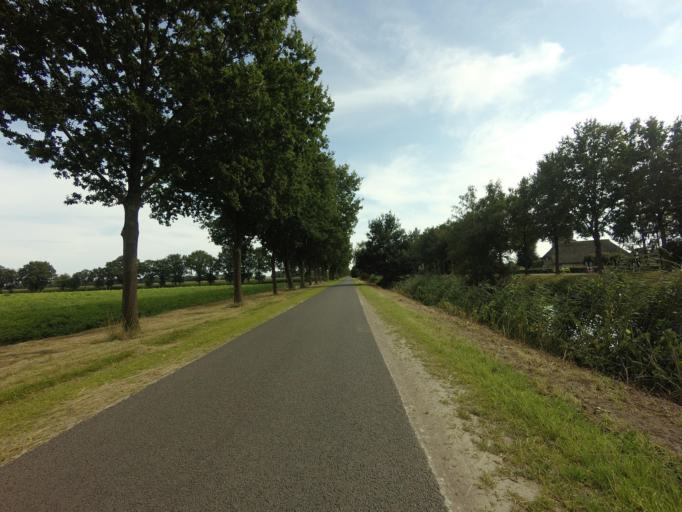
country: NL
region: Drenthe
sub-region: Gemeente Coevorden
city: Coevorden
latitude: 52.6851
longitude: 6.7128
